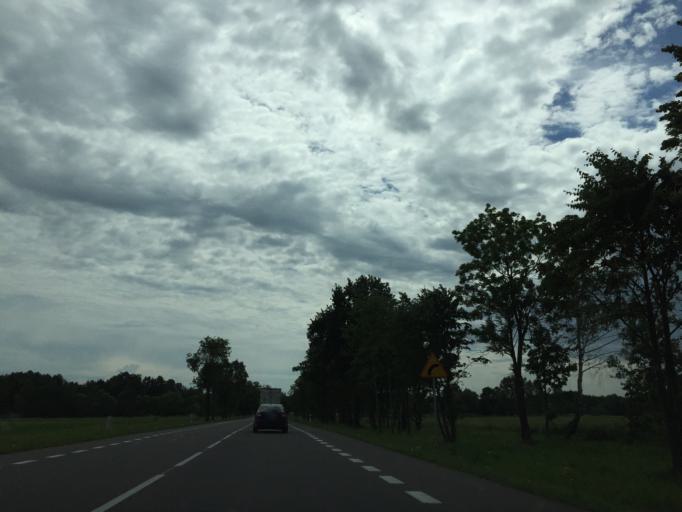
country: PL
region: Podlasie
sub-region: Powiat bielski
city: Bielsk Podlaski
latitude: 52.7386
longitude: 23.1642
